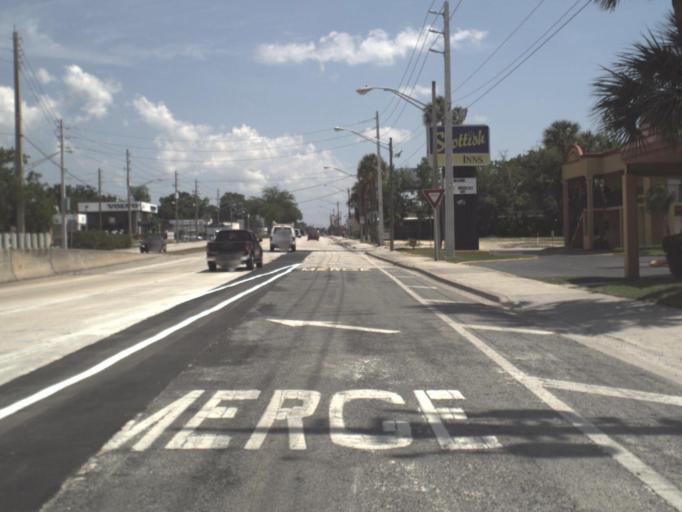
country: US
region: Florida
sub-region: Duval County
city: Jacksonville
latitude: 30.3053
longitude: -81.6453
